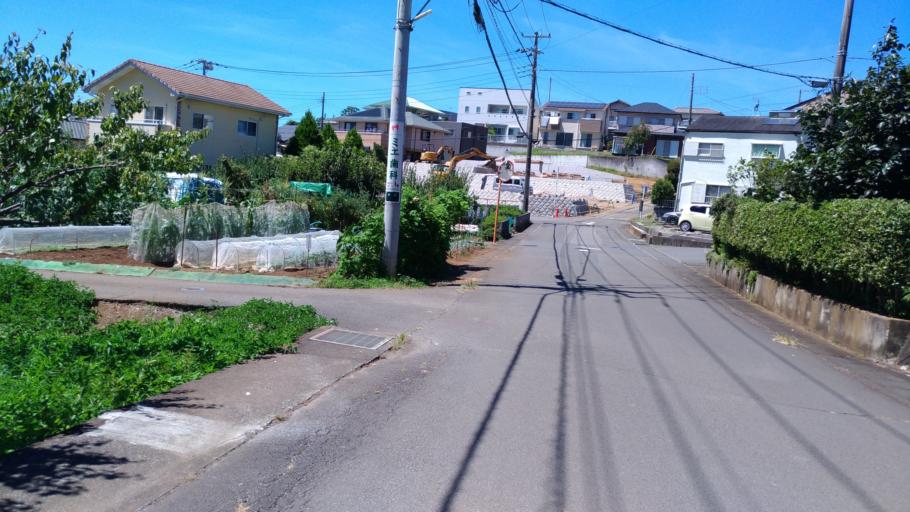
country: JP
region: Shizuoka
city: Mishima
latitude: 35.0844
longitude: 138.9532
